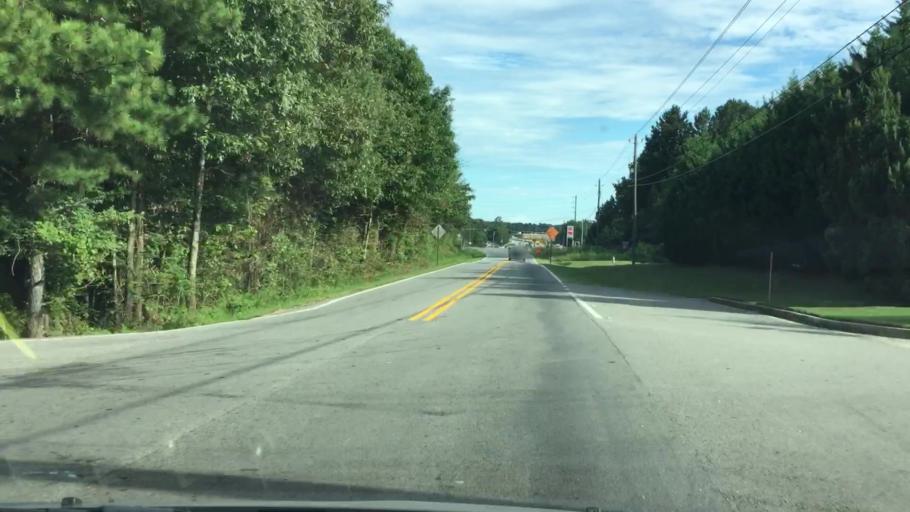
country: US
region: Georgia
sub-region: Clayton County
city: Conley
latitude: 33.6288
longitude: -84.2581
